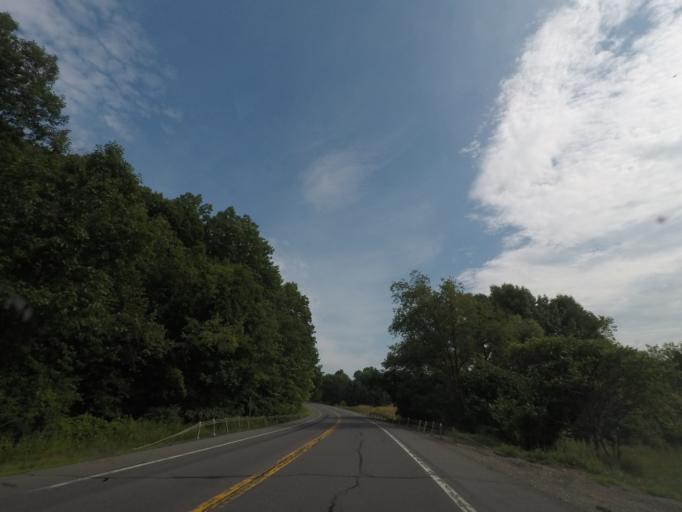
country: US
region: New York
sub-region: Rensselaer County
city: Poestenkill
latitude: 42.6960
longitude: -73.5600
